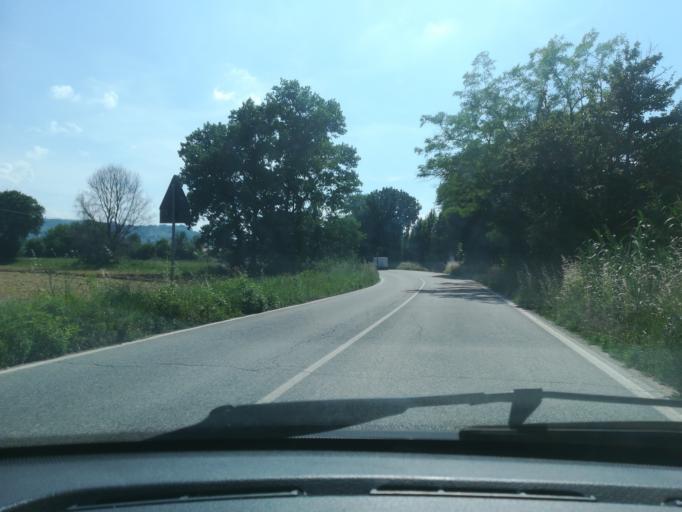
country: IT
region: The Marches
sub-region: Provincia di Macerata
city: Pollenza
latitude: 43.2938
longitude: 13.3710
